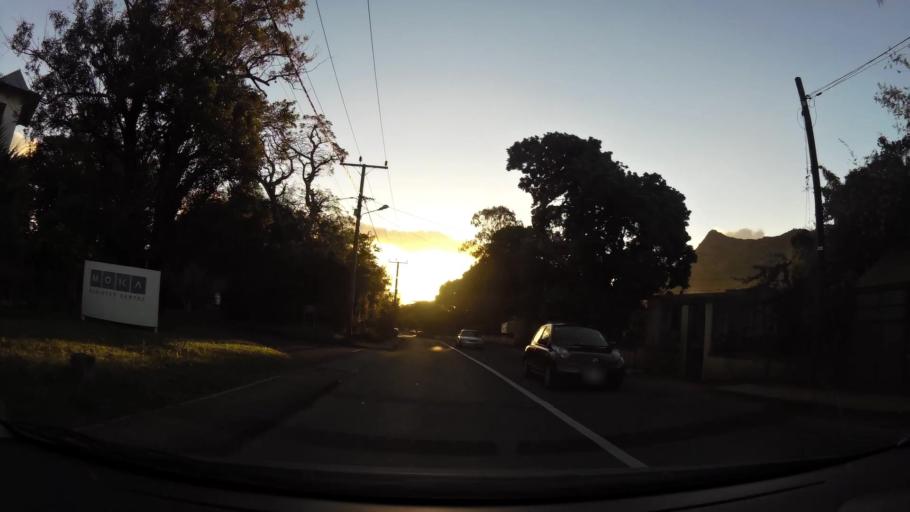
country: MU
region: Moka
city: Moka
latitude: -20.2246
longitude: 57.5061
